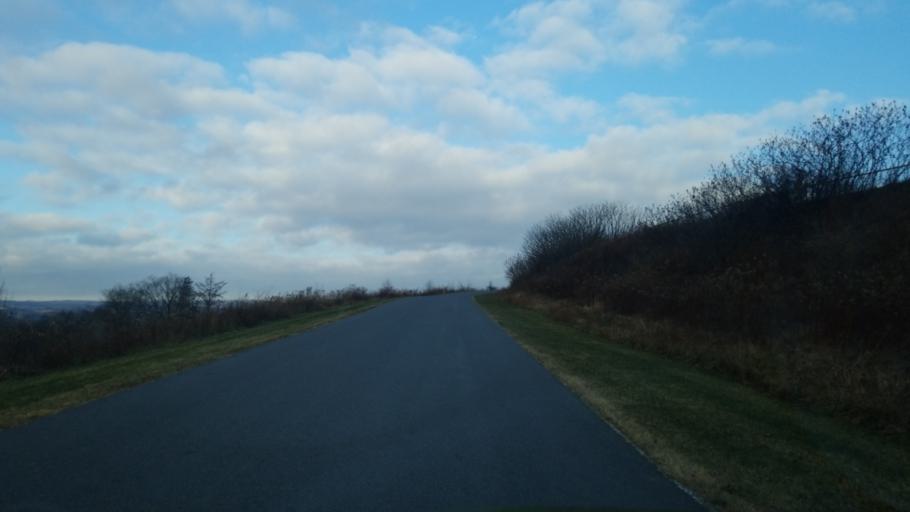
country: US
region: Pennsylvania
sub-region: Clearfield County
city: Clearfield
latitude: 41.0081
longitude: -78.4225
